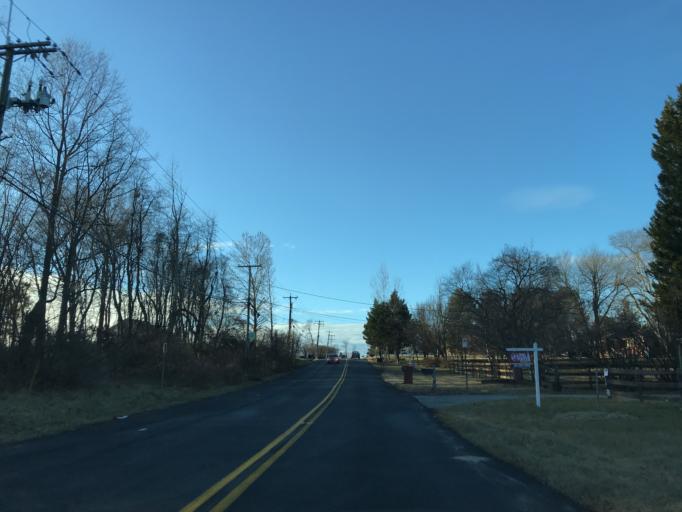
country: US
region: Maryland
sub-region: Montgomery County
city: Burtonsville
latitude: 39.0969
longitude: -76.9409
